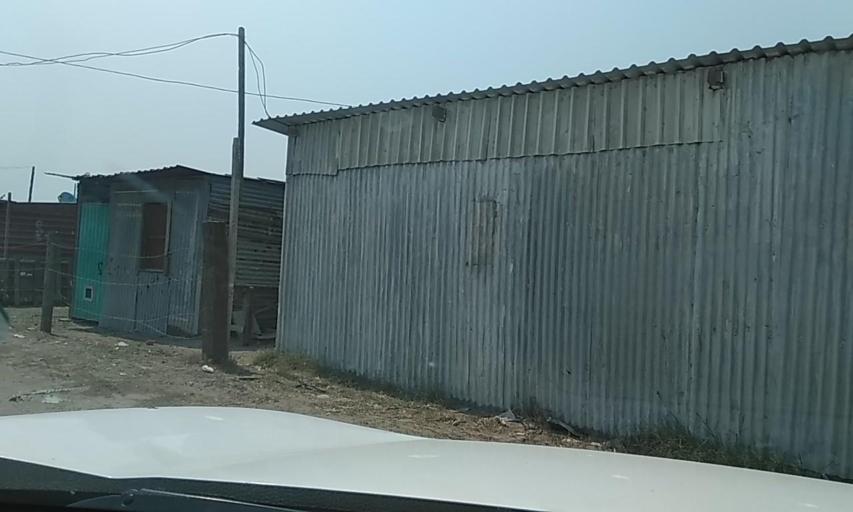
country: MX
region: Veracruz
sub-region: Veracruz
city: Las Amapolas
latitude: 19.1773
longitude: -96.1780
